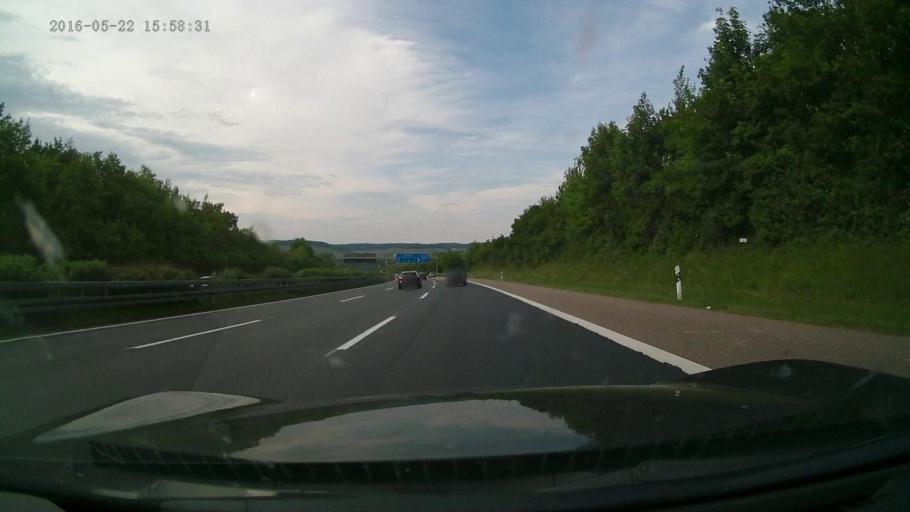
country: DE
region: Baden-Wuerttemberg
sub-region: Regierungsbezirk Stuttgart
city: Ellhofen
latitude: 49.1418
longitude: 9.3063
